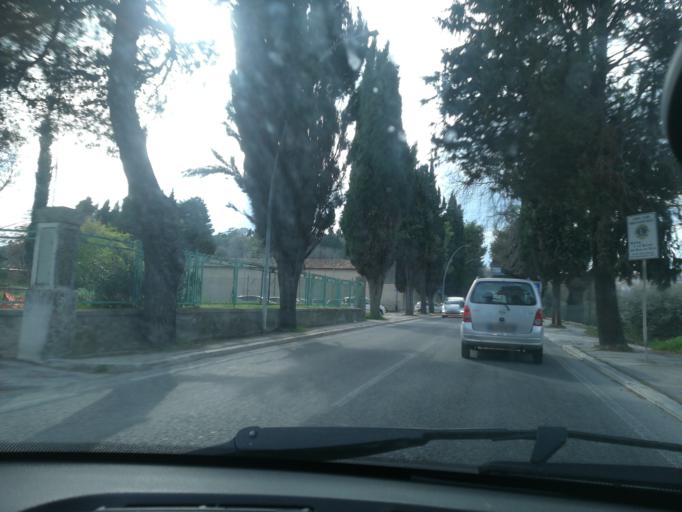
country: IT
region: The Marches
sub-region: Provincia di Macerata
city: Macerata
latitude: 43.2941
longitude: 13.4670
